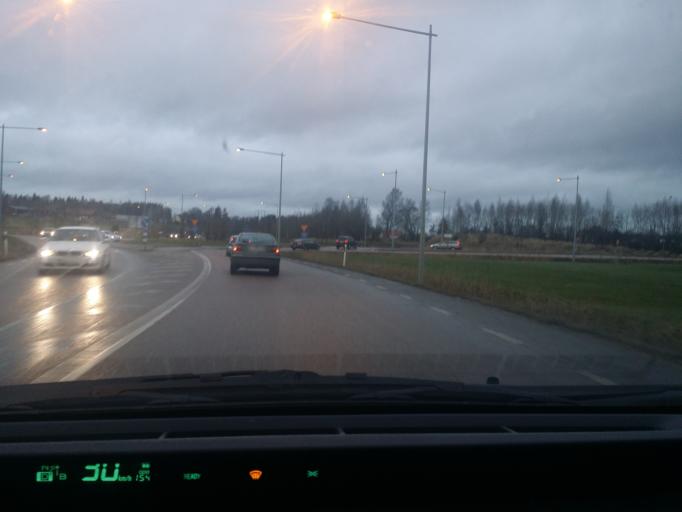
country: SE
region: Soedermanland
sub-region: Eskilstuna Kommun
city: Torshalla
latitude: 59.3750
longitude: 16.4649
